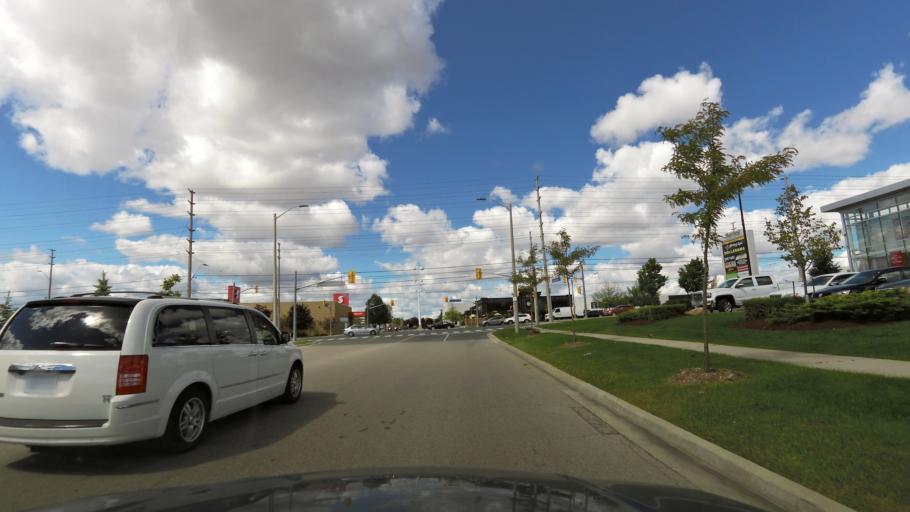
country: CA
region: Ontario
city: Mississauga
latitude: 43.6087
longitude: -79.6983
